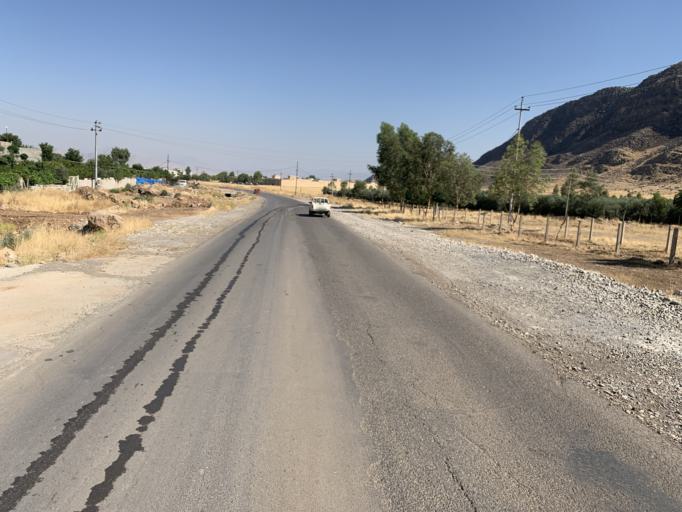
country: IQ
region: As Sulaymaniyah
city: Raniye
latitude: 36.2677
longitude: 44.8389
